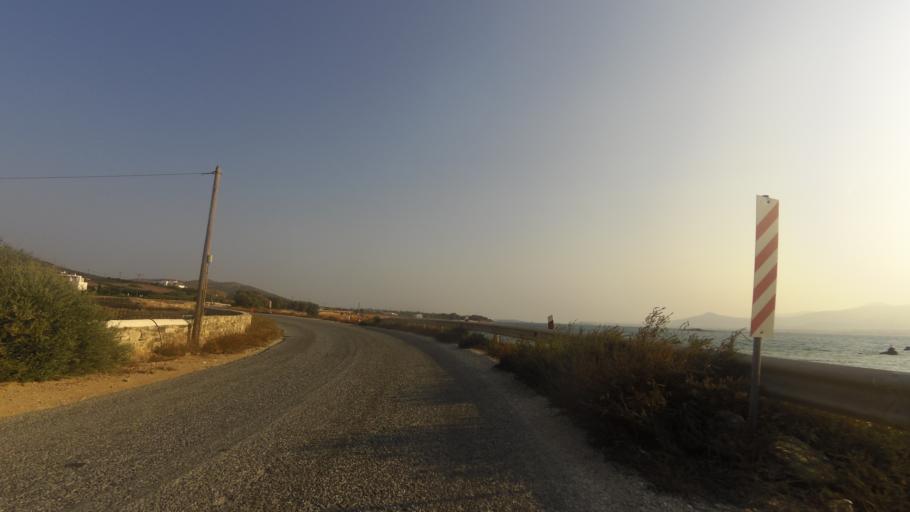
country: GR
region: South Aegean
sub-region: Nomos Kykladon
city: Antiparos
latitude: 37.0123
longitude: 25.0755
